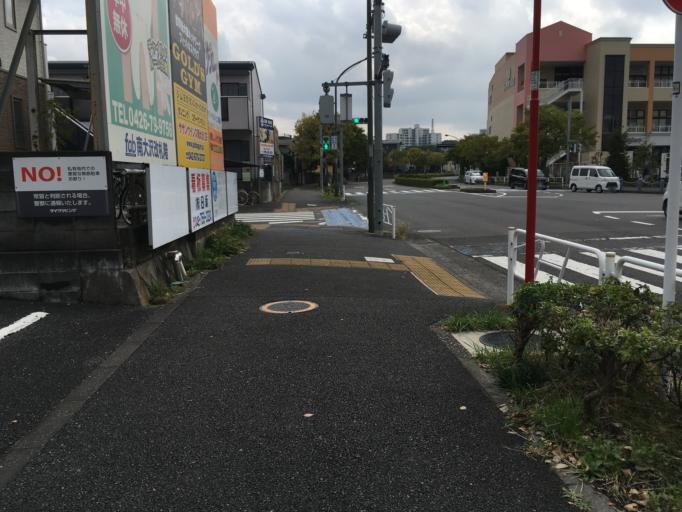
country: JP
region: Tokyo
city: Hino
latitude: 35.6140
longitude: 139.3818
